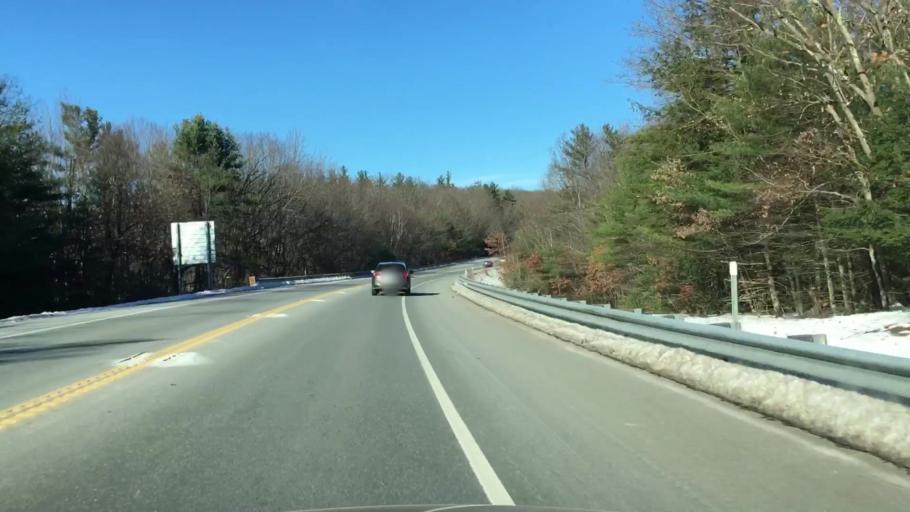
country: US
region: New Hampshire
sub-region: Hillsborough County
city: Milford
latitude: 42.8381
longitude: -71.6191
